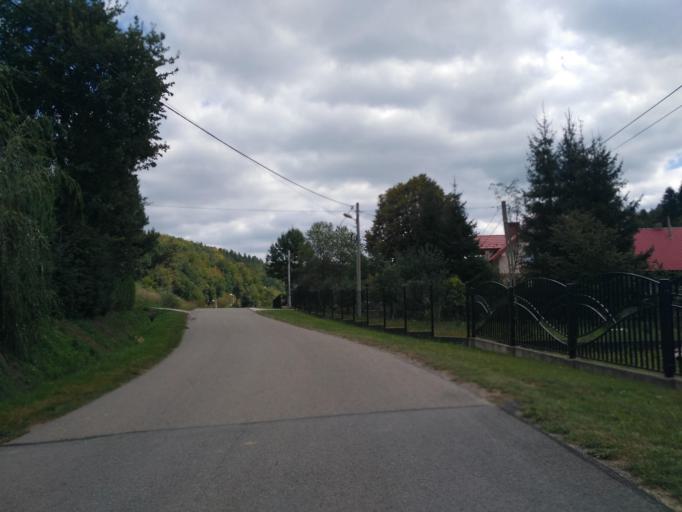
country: PL
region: Subcarpathian Voivodeship
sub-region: Powiat rzeszowski
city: Dynow
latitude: 49.7726
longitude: 22.2475
